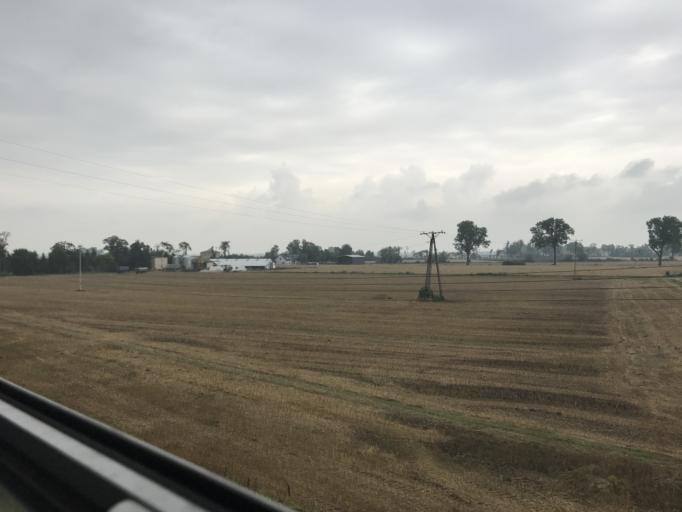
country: PL
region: Pomeranian Voivodeship
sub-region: Powiat tczewski
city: Tczew
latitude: 54.1147
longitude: 18.7734
